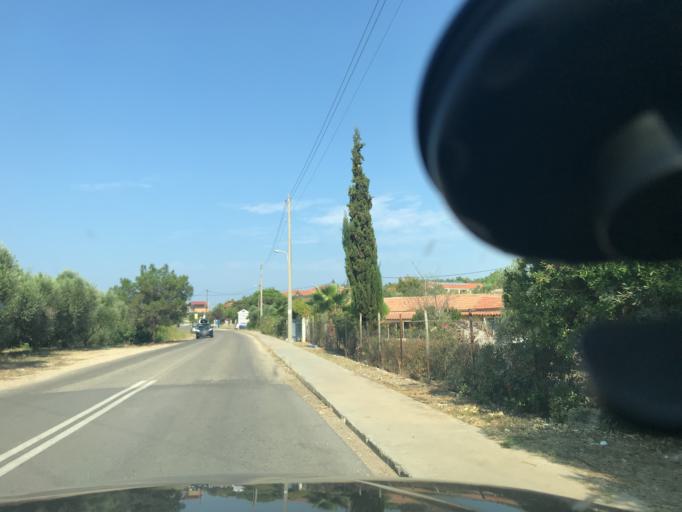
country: GR
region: West Greece
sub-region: Nomos Ileias
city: Kardamas
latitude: 37.7152
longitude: 21.3458
